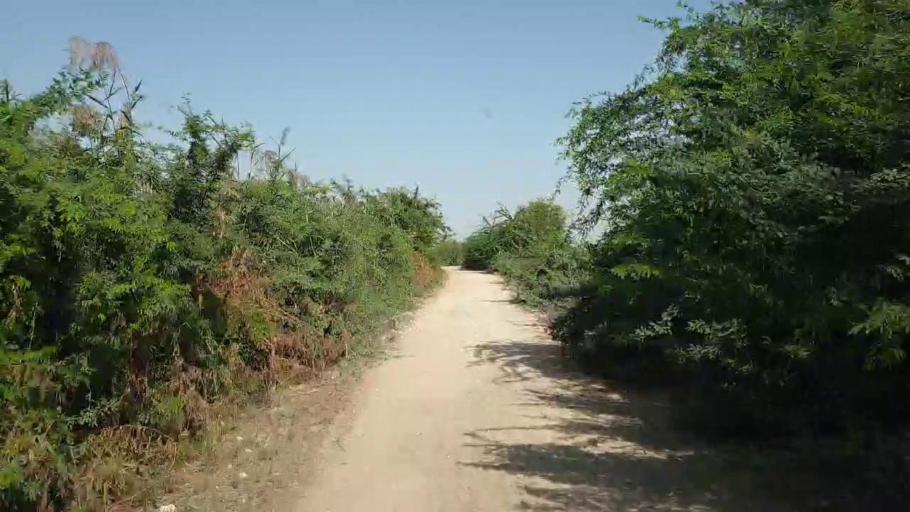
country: PK
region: Sindh
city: Tando Bago
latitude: 24.7493
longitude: 69.0302
